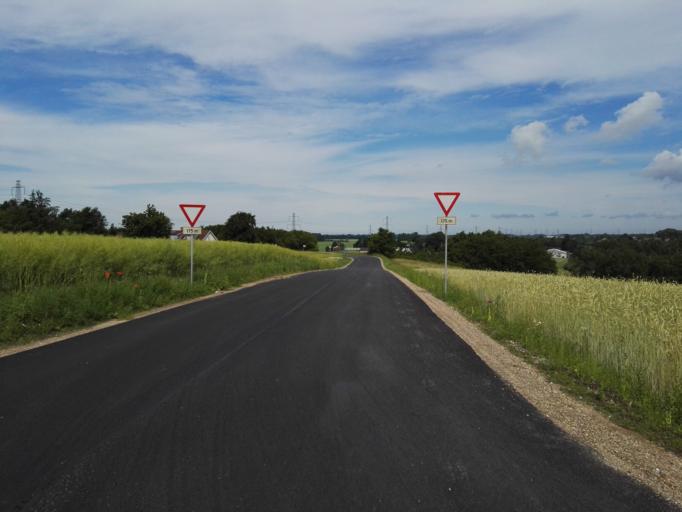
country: DK
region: Capital Region
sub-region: Egedal Kommune
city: Olstykke
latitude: 55.8217
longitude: 12.1668
